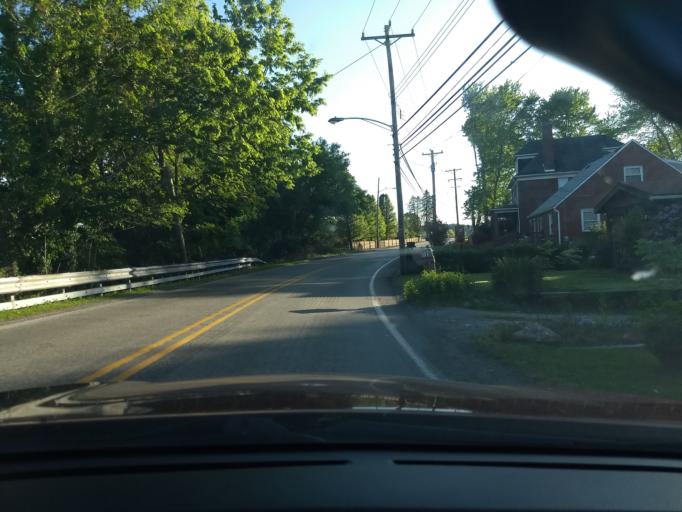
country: US
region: Pennsylvania
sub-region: Allegheny County
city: Versailles
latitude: 40.3194
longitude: -79.8219
